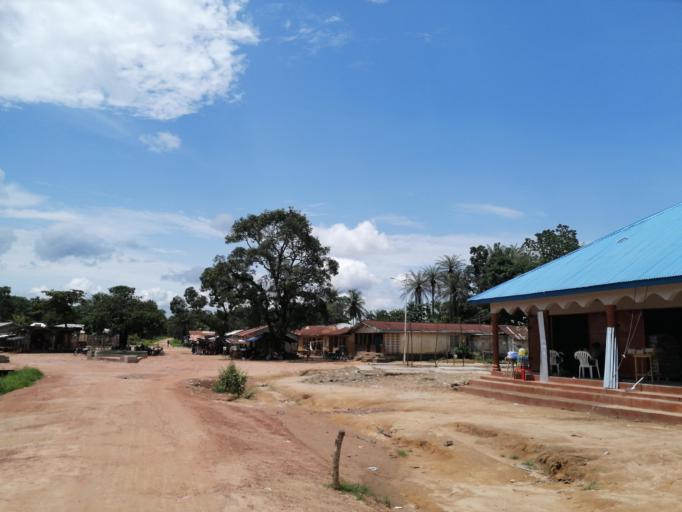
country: SL
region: Northern Province
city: Konakridee
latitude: 8.7768
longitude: -13.1356
